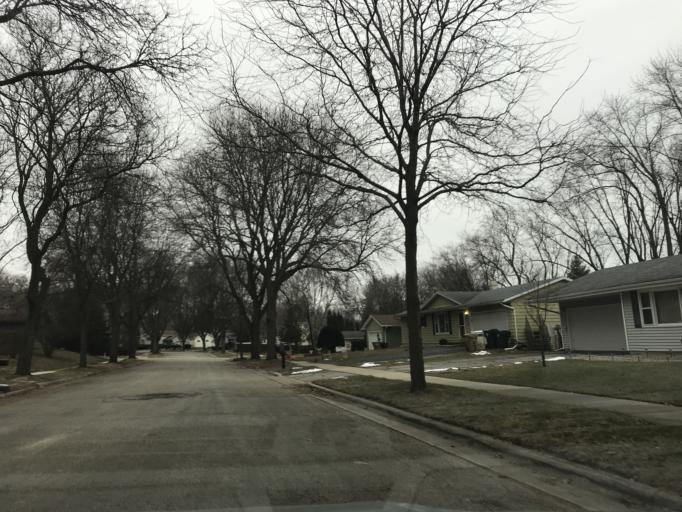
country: US
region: Wisconsin
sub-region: Dane County
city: Monona
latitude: 43.1015
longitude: -89.3003
